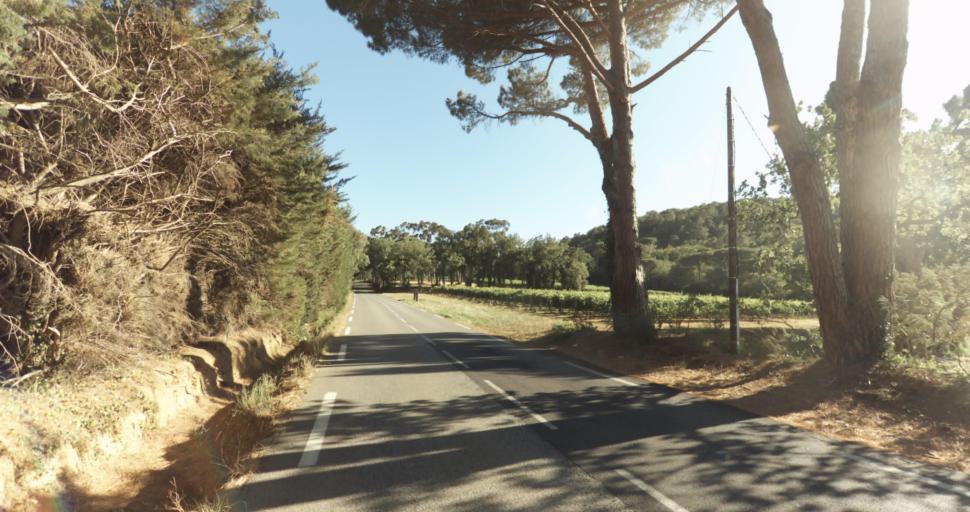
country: FR
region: Provence-Alpes-Cote d'Azur
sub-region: Departement du Var
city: Gassin
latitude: 43.2499
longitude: 6.5906
